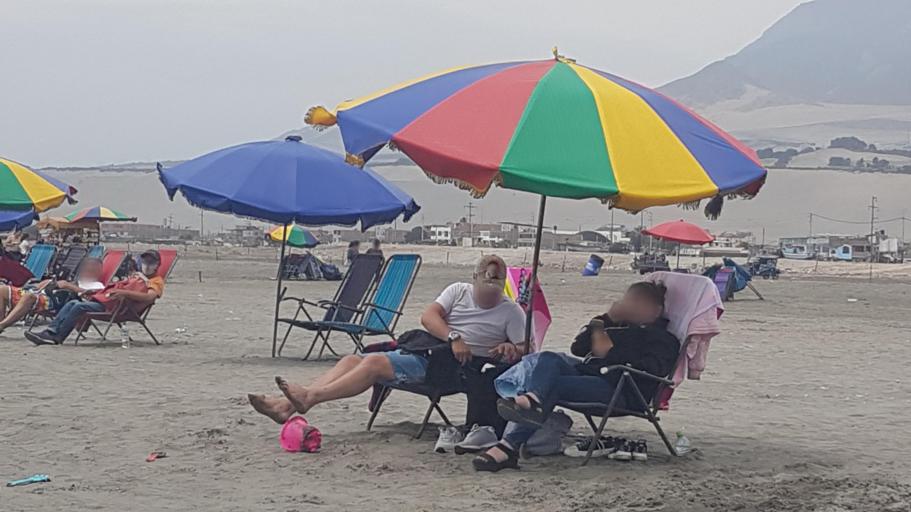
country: PE
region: La Libertad
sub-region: Provincia de Trujillo
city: Salaverry
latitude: -8.2219
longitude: -78.9820
